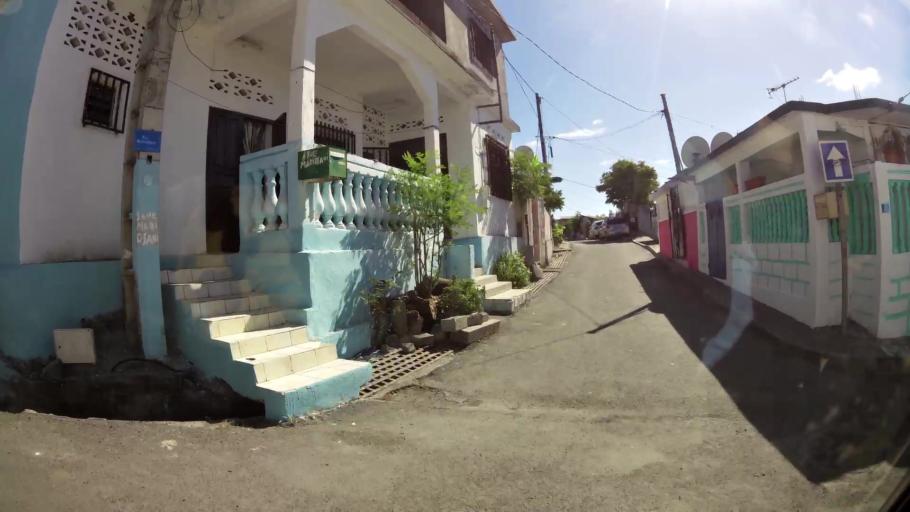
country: YT
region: Pamandzi
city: Pamandzi
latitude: -12.7879
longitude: 45.2703
